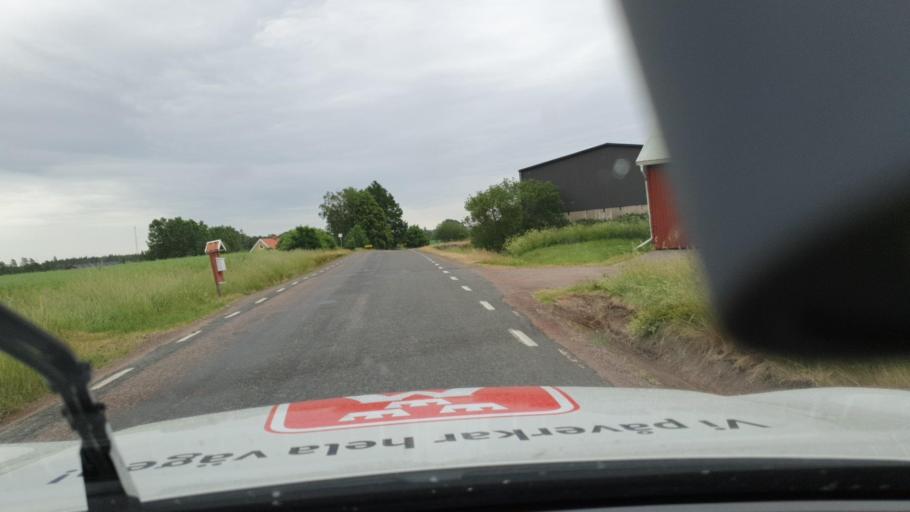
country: SE
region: Vaestra Goetaland
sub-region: Tidaholms Kommun
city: Olofstorp
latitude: 58.3339
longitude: 14.0547
